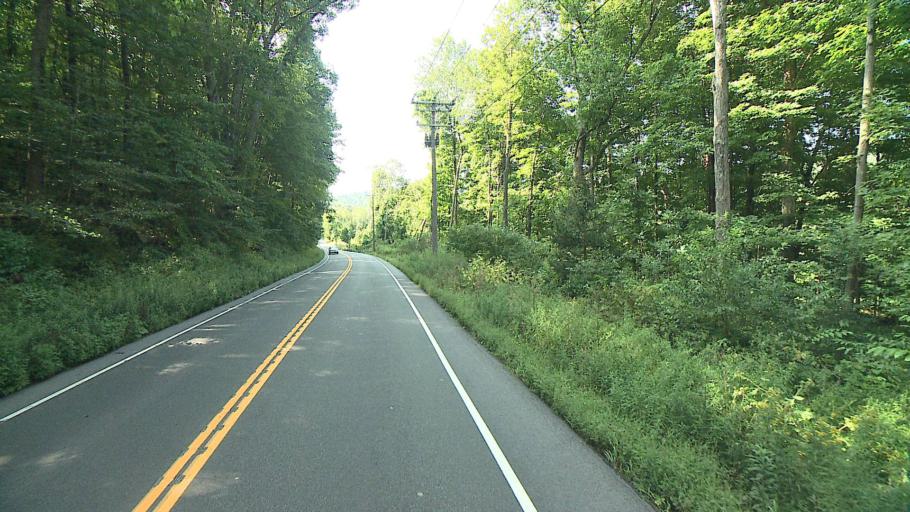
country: US
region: Connecticut
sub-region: Litchfield County
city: Kent
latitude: 41.6567
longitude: -73.4896
